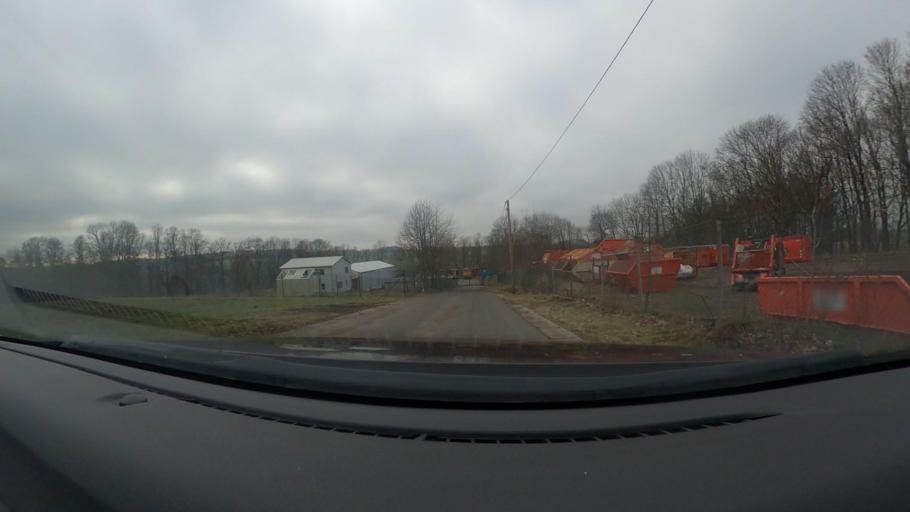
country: DE
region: Saxony
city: Oberschona
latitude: 50.9006
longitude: 13.2537
